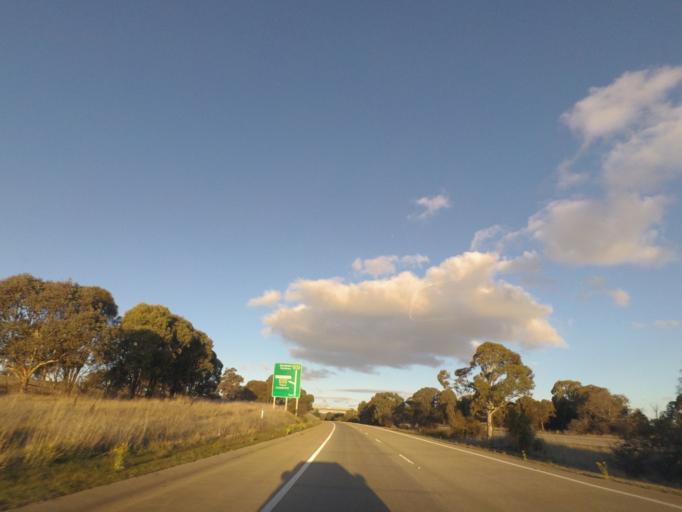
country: AU
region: New South Wales
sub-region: Yass Valley
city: Yass
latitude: -34.8120
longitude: 148.9388
